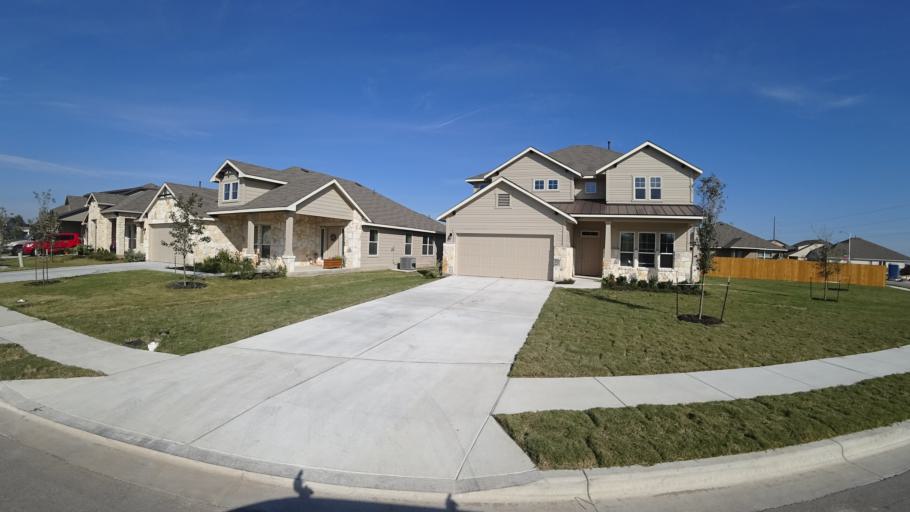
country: US
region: Texas
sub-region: Travis County
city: Pflugerville
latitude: 30.4087
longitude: -97.6414
